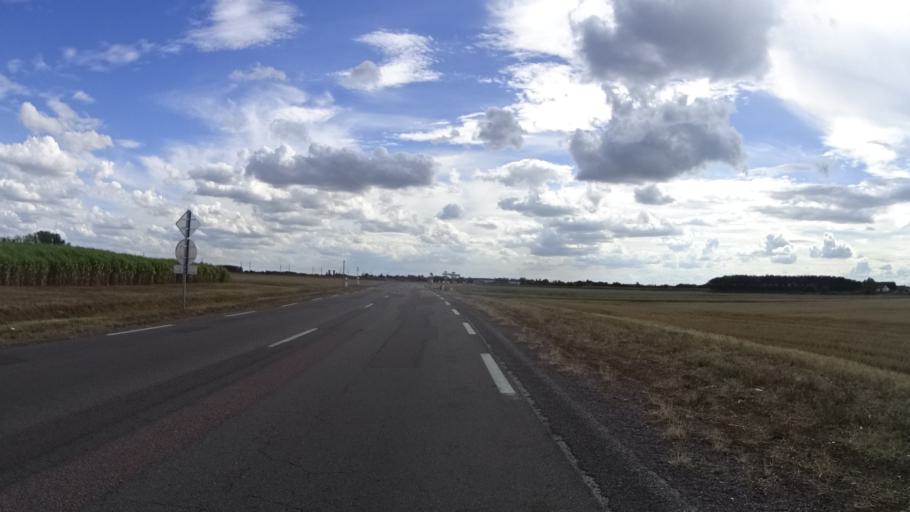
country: FR
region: Bourgogne
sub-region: Departement de la Cote-d'Or
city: Seurre
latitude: 47.0197
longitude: 5.1644
